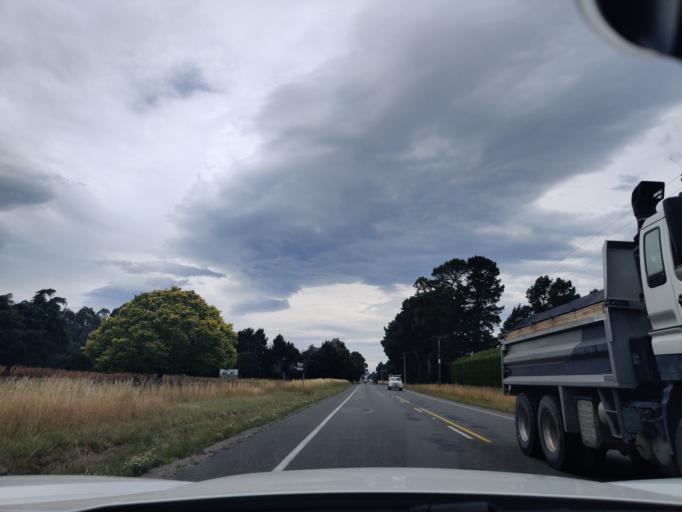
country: NZ
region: Wellington
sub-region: Masterton District
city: Masterton
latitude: -40.9866
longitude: 175.5768
